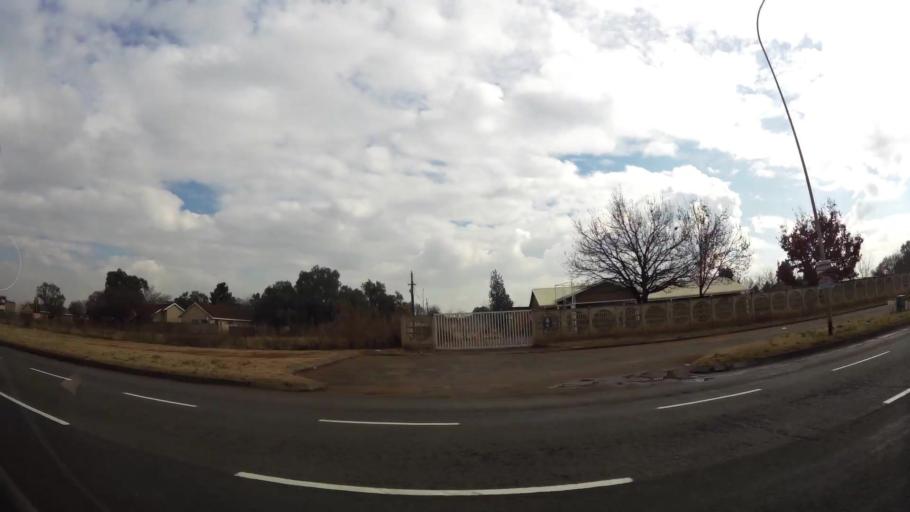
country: ZA
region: Gauteng
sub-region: Sedibeng District Municipality
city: Meyerton
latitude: -26.5928
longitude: 27.9966
